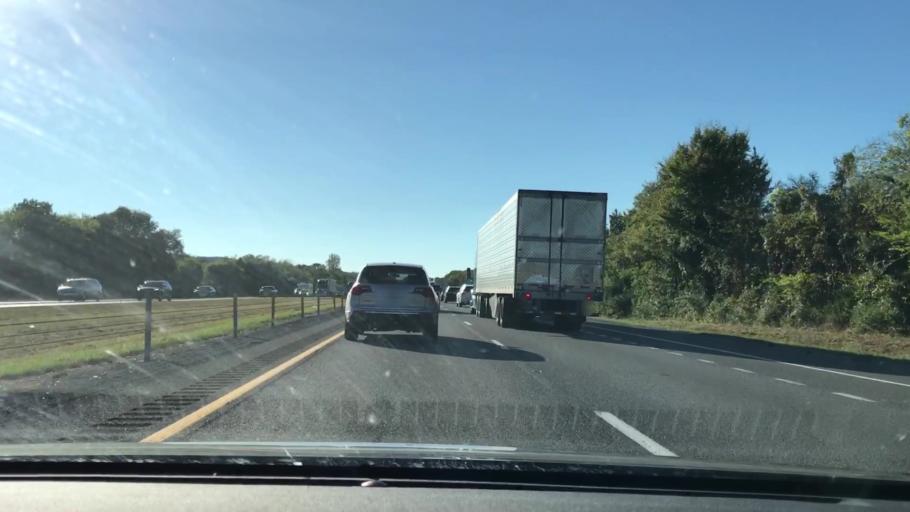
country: US
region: Tennessee
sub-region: Wilson County
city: Lebanon
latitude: 36.1839
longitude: -86.3341
